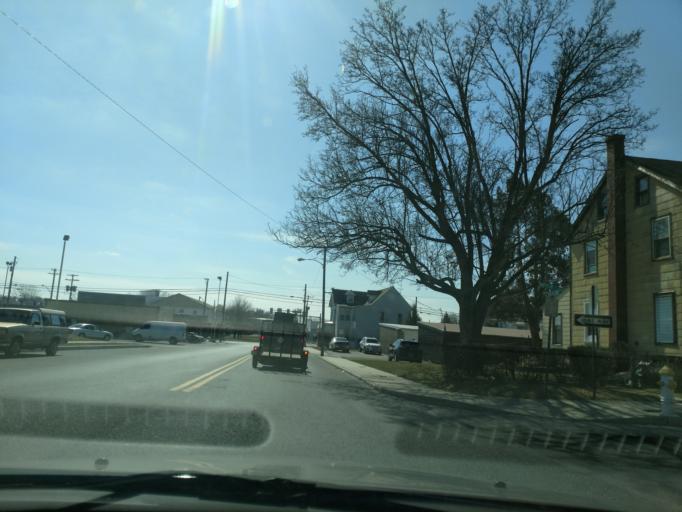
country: US
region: Pennsylvania
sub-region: Lebanon County
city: Lebanon
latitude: 40.3473
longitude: -76.4115
